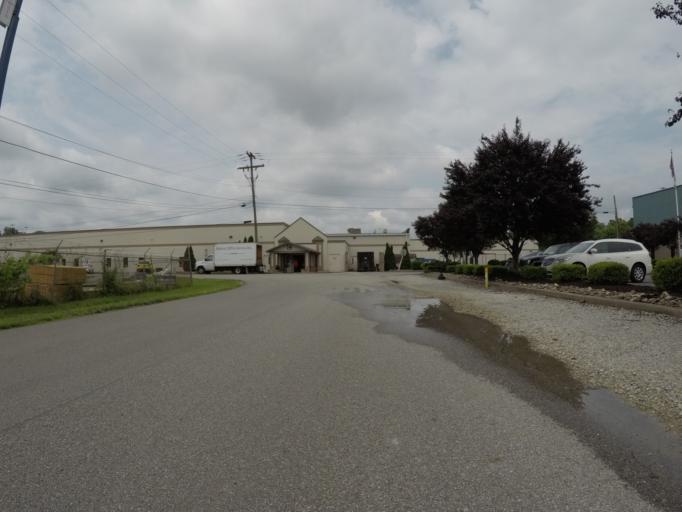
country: US
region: West Virginia
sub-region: Cabell County
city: Pea Ridge
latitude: 38.4155
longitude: -82.3438
